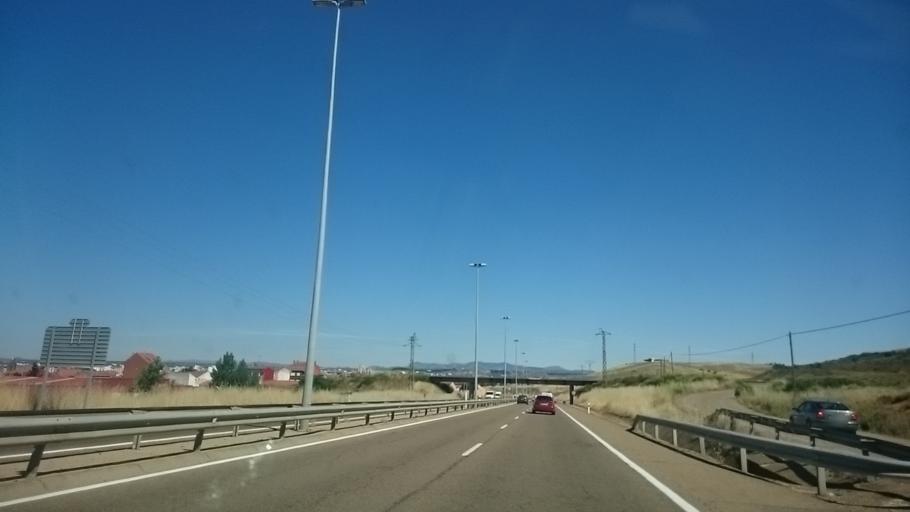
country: ES
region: Castille and Leon
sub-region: Provincia de Leon
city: Leon
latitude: 42.5798
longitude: -5.5456
